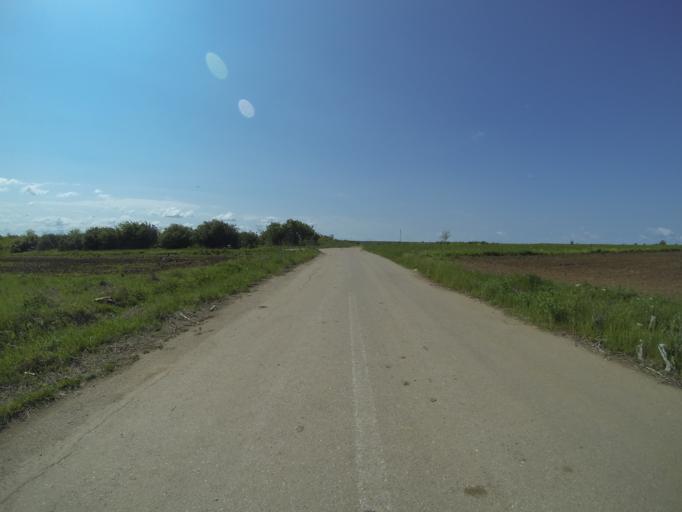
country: RO
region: Dolj
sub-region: Comuna Orodelu
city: Orodelu
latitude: 44.2486
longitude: 23.2515
